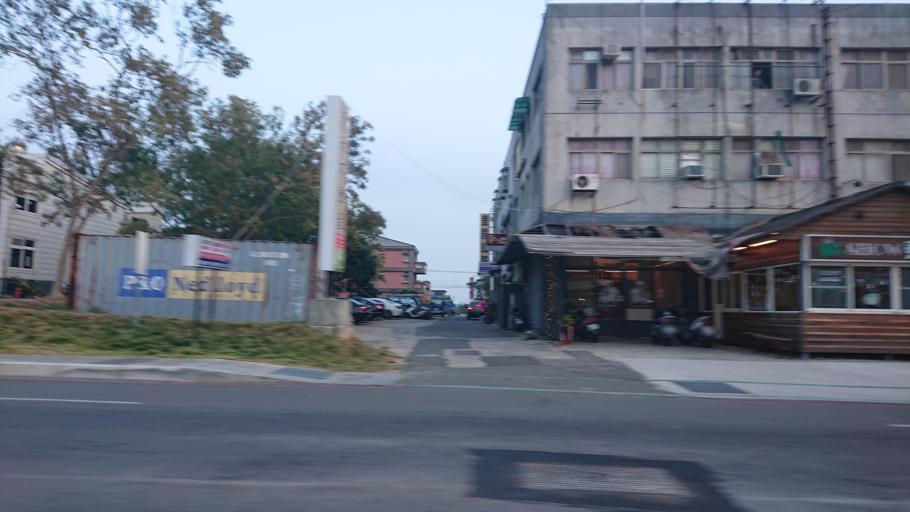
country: TW
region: Fukien
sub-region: Kinmen
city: Jincheng
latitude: 24.4406
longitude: 118.3219
